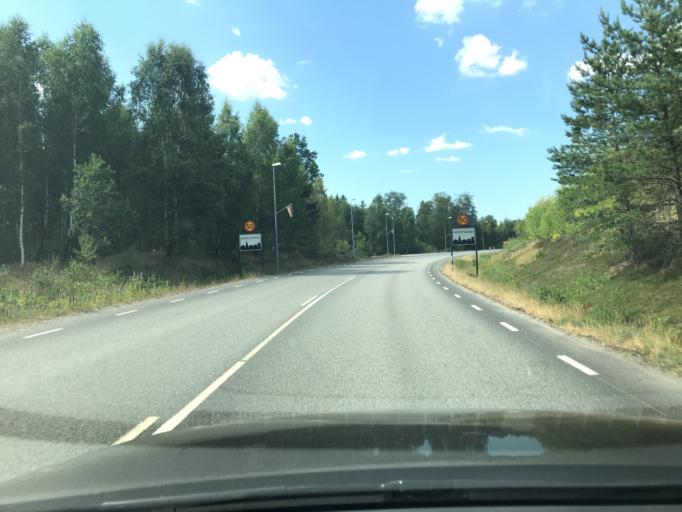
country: SE
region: Skane
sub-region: Hassleholms Kommun
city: Hastveda
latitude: 56.2787
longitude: 13.9338
